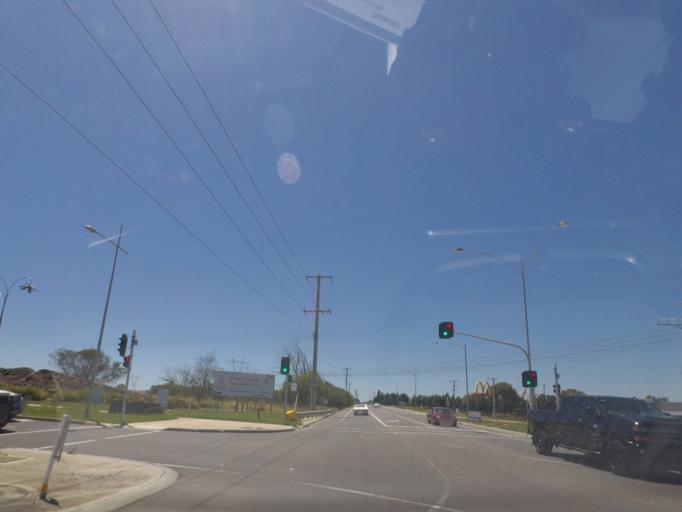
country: AU
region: Victoria
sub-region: Whittlesea
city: Epping
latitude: -37.6230
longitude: 145.0287
